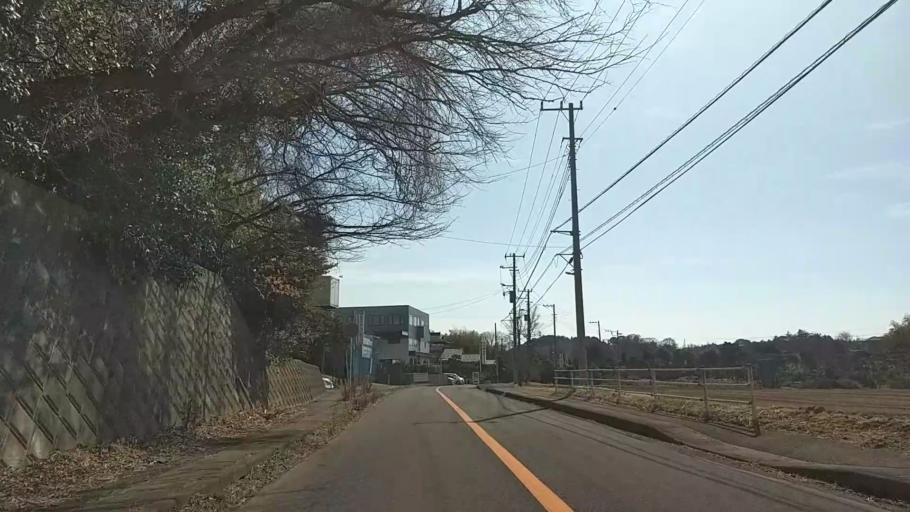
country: JP
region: Kanagawa
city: Fujisawa
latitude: 35.3824
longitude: 139.4299
